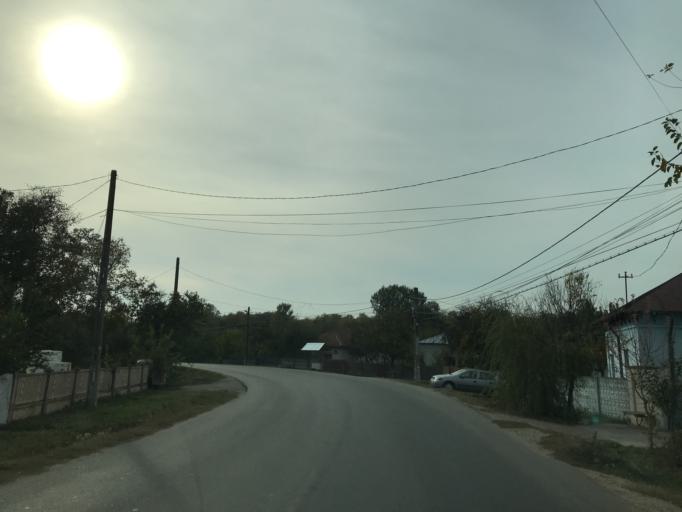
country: RO
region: Olt
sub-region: Comuna Piatra Olt
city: Piatra
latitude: 44.3662
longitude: 24.3002
